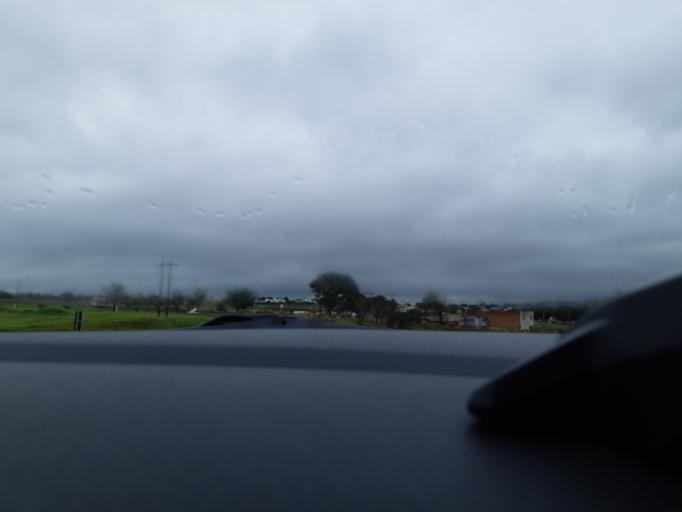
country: BR
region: Sao Paulo
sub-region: Ourinhos
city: Ourinhos
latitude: -22.9760
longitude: -49.9018
